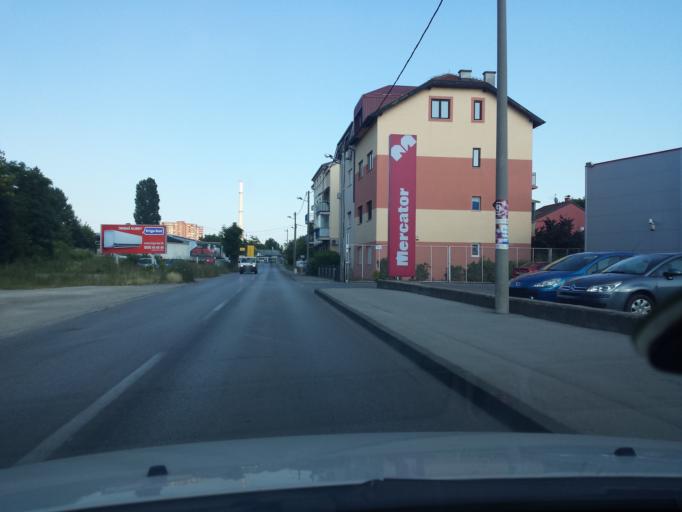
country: HR
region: Grad Zagreb
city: Jankomir
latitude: 45.8090
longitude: 15.9310
